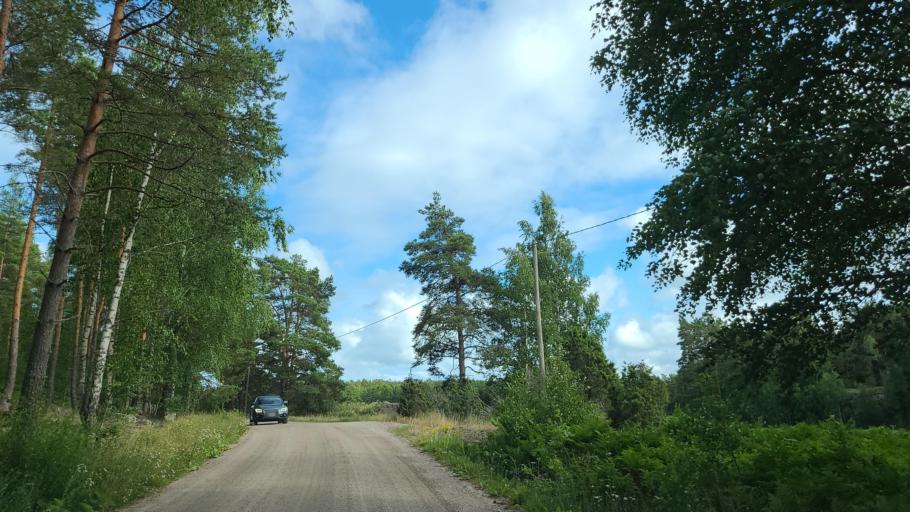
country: FI
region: Varsinais-Suomi
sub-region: Aboland-Turunmaa
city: Nagu
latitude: 60.1420
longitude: 21.7889
